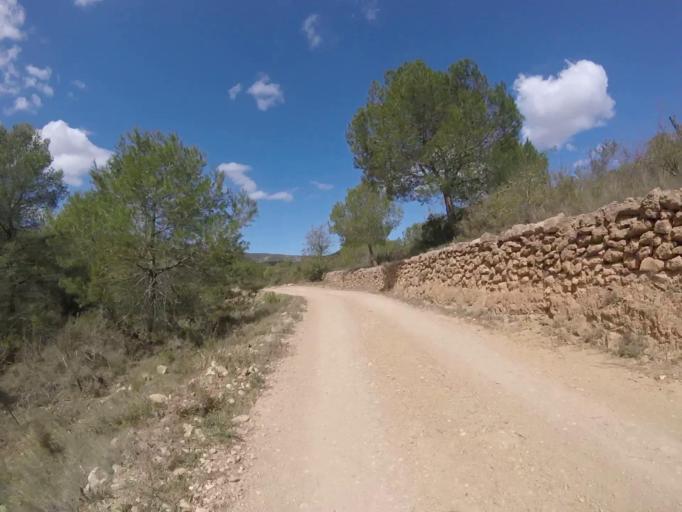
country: ES
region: Valencia
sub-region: Provincia de Castello
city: Santa Magdalena de Pulpis
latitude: 40.3237
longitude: 0.3441
